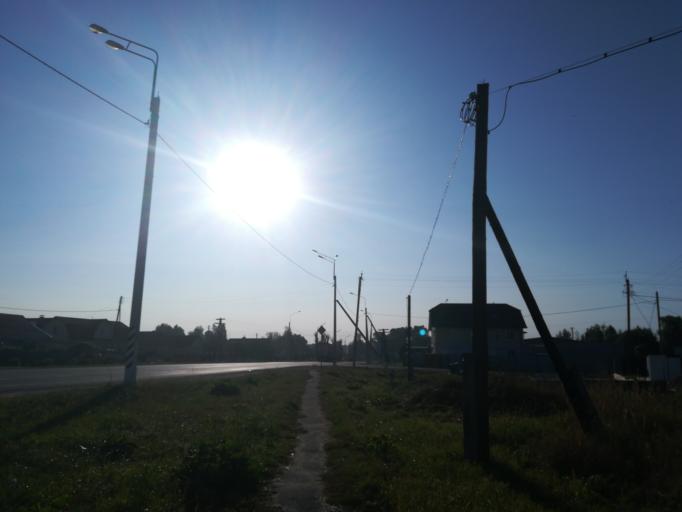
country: RU
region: Brjansk
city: Karachev
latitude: 53.1271
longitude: 34.9411
